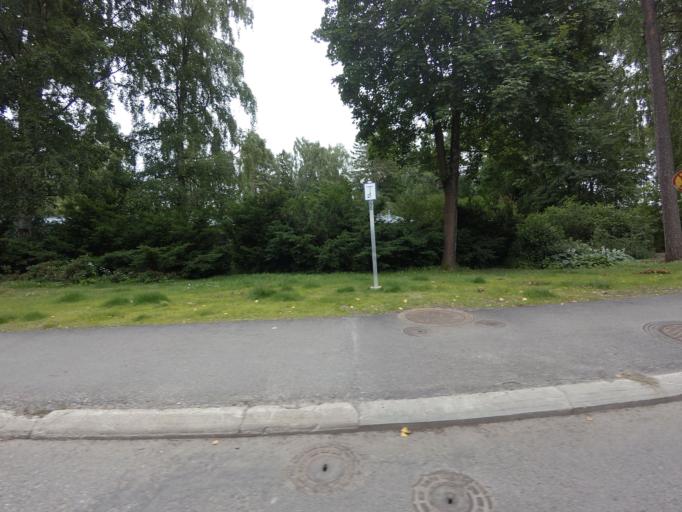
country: FI
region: Uusimaa
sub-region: Helsinki
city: Otaniemi
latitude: 60.1722
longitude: 24.8233
